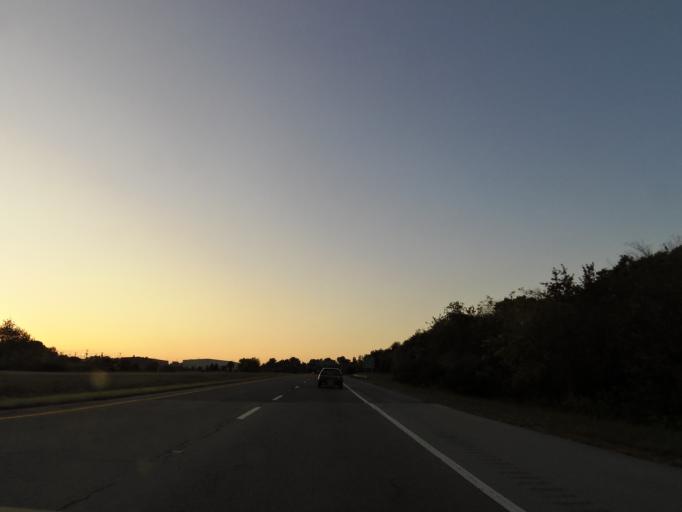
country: US
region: Tennessee
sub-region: Blount County
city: Alcoa
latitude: 35.8313
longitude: -83.9635
